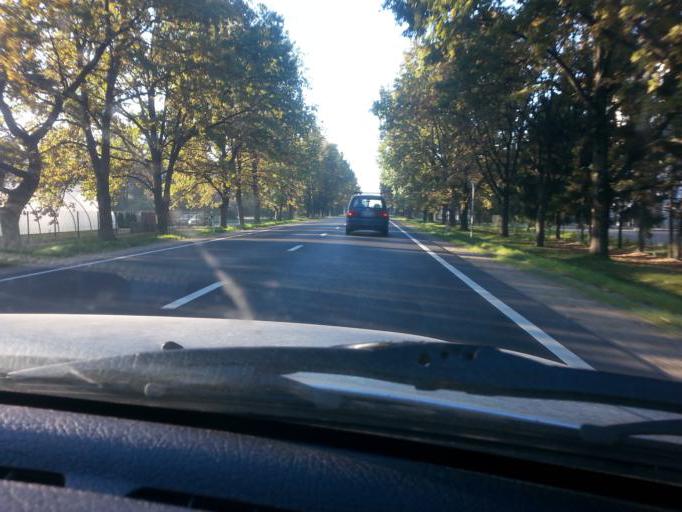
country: LT
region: Siauliu apskritis
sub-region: Joniskis
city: Joniskis
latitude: 56.4201
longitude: 23.6843
